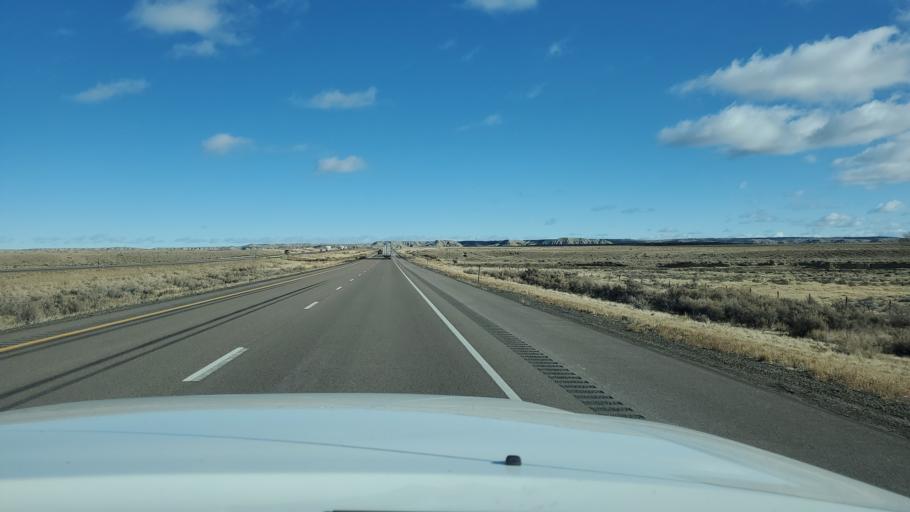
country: US
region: Wyoming
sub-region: Uinta County
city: Lyman
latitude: 41.3882
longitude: -110.2039
